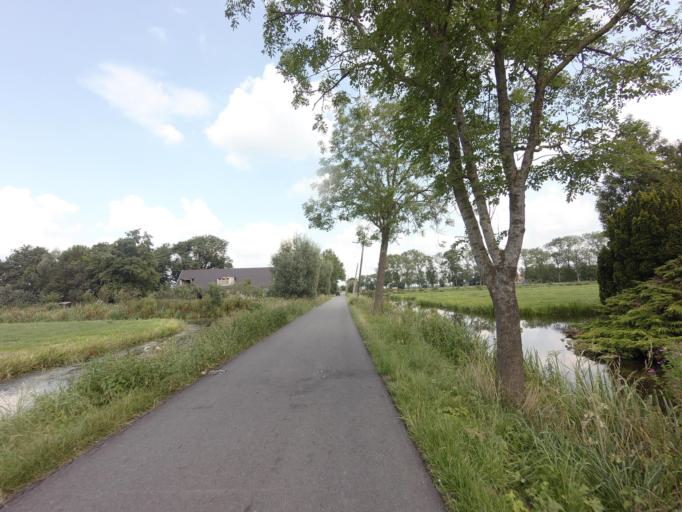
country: NL
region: South Holland
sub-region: Gemeente Vlist
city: Vlist
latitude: 51.9651
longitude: 4.8022
